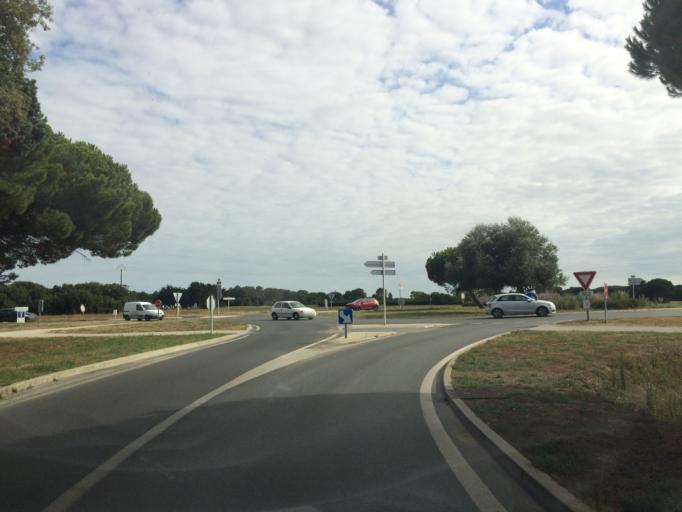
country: FR
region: Poitou-Charentes
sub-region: Departement de la Charente-Maritime
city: La Flotte
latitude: 46.1799
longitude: -1.3330
